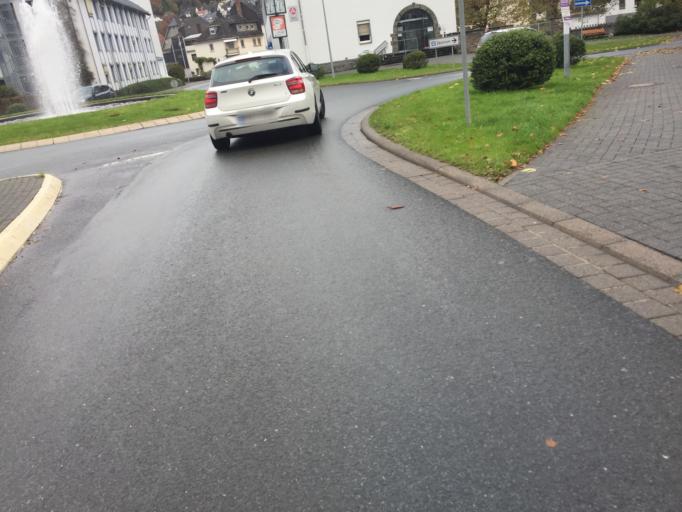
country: DE
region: Hesse
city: Dillenburg
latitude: 50.7401
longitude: 8.2835
